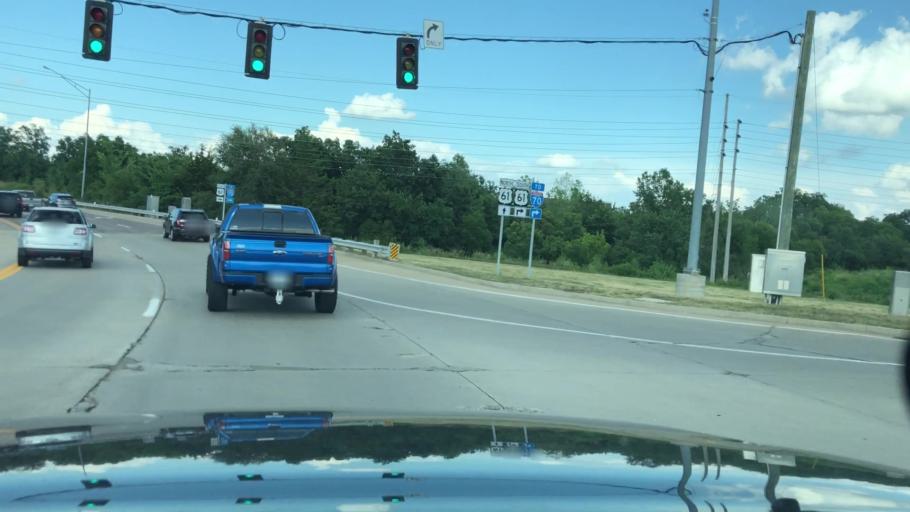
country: US
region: Missouri
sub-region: Saint Charles County
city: Wentzville
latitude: 38.8217
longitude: -90.8507
